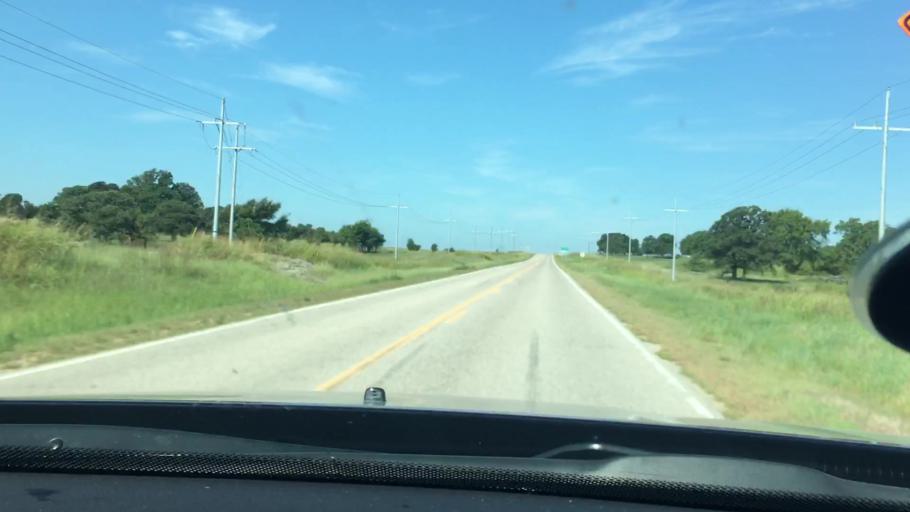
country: US
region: Oklahoma
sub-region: Johnston County
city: Tishomingo
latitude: 34.3613
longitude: -96.6269
